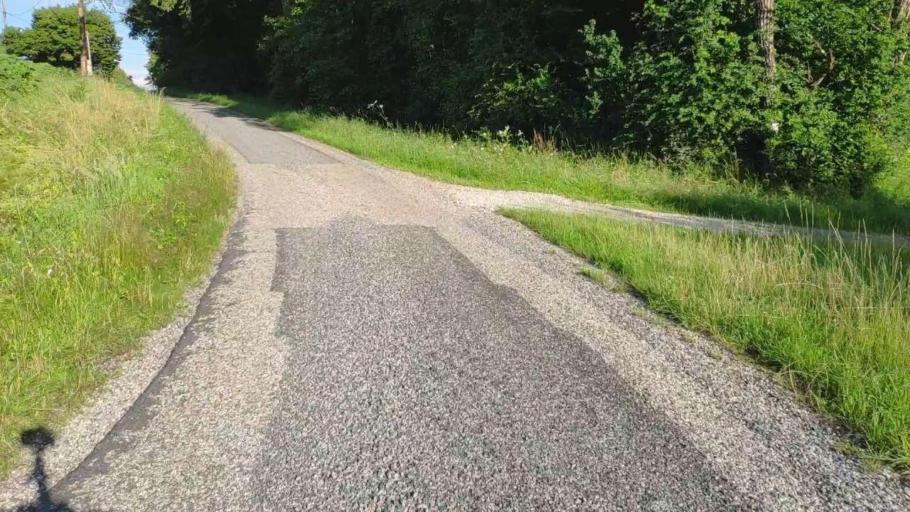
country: FR
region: Franche-Comte
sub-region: Departement du Jura
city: Bletterans
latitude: 46.7962
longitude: 5.4816
